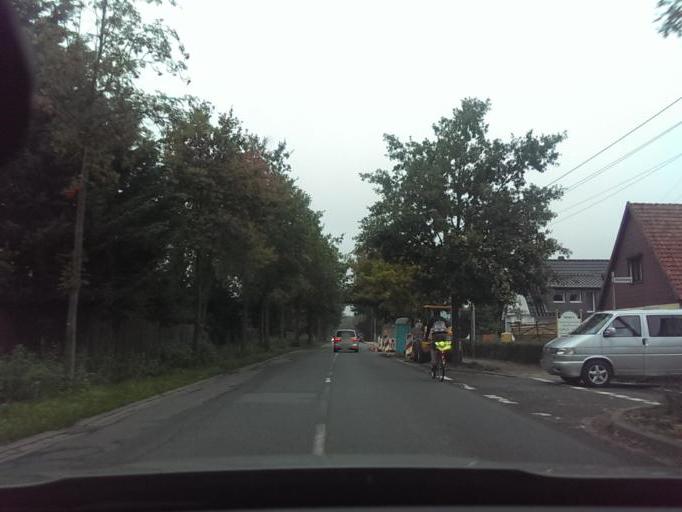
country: DE
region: Lower Saxony
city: Garbsen-Mitte
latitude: 52.4984
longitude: 9.6312
